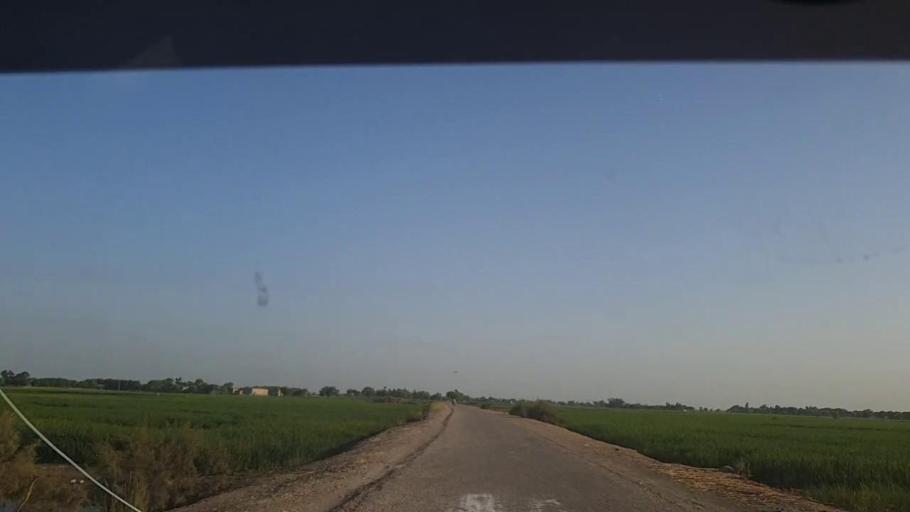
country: PK
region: Sindh
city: Thul
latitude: 28.2145
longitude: 68.8694
